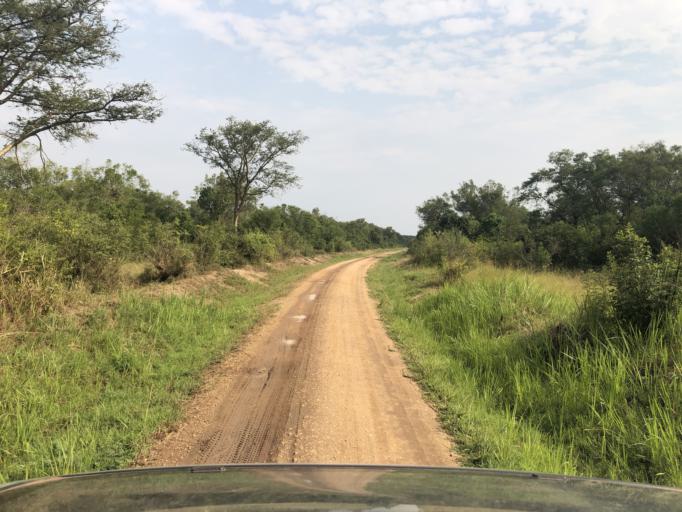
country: UG
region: Western Region
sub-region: Rubirizi District
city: Rubirizi
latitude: -0.4366
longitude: 29.7906
